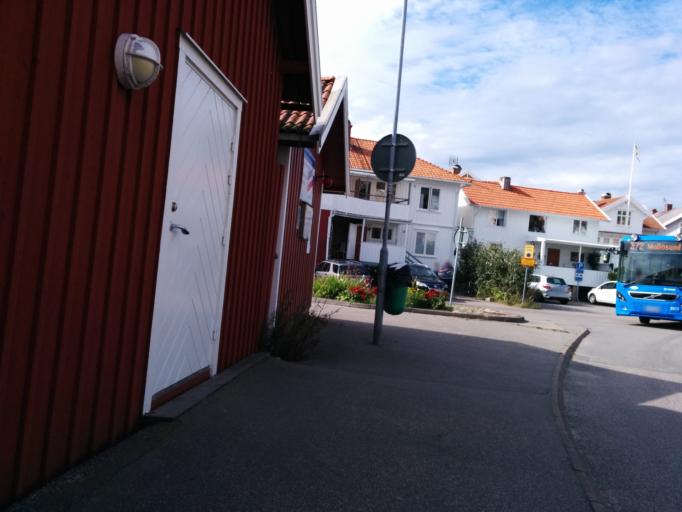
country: SE
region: Vaestra Goetaland
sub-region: Lysekils Kommun
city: Lysekil
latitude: 58.1228
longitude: 11.4437
